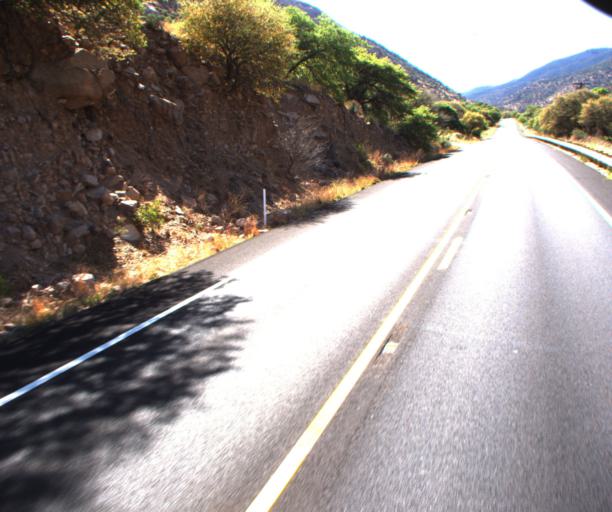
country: US
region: Arizona
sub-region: Cochise County
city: Bisbee
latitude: 31.4885
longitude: -109.9880
